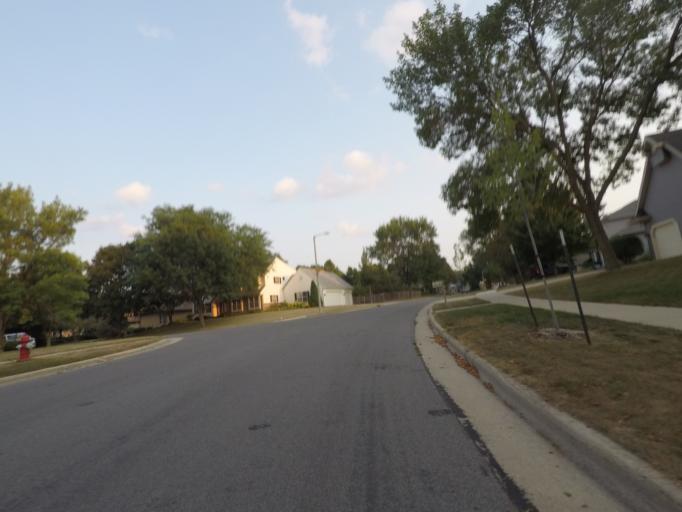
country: US
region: Wisconsin
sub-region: Dane County
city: Middleton
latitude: 43.0703
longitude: -89.5164
